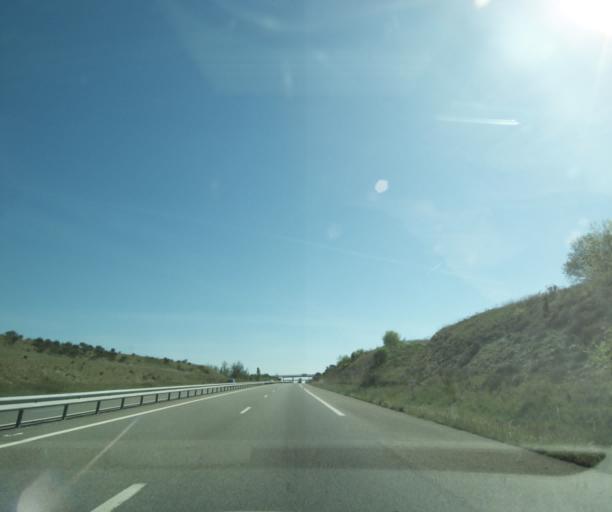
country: FR
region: Midi-Pyrenees
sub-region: Departement du Lot
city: Lalbenque
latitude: 44.3484
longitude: 1.4991
